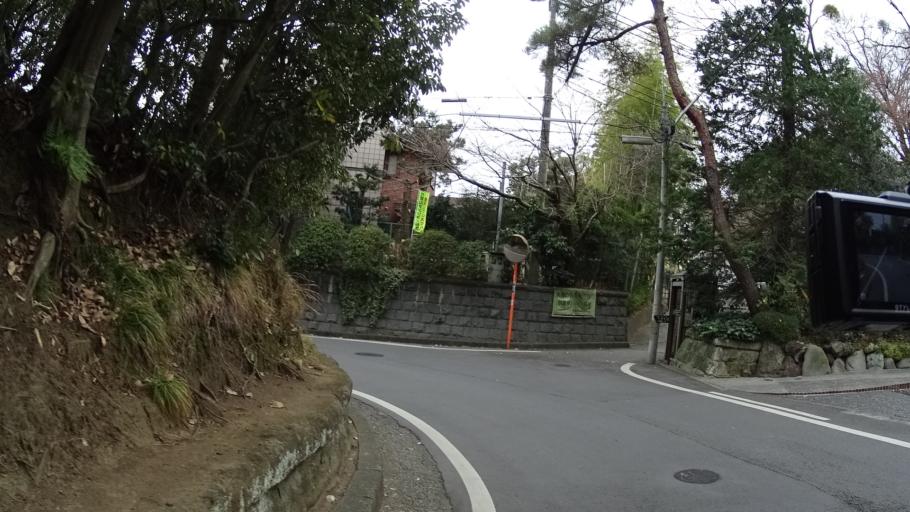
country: JP
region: Kanagawa
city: Oiso
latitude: 35.3112
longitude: 139.3077
